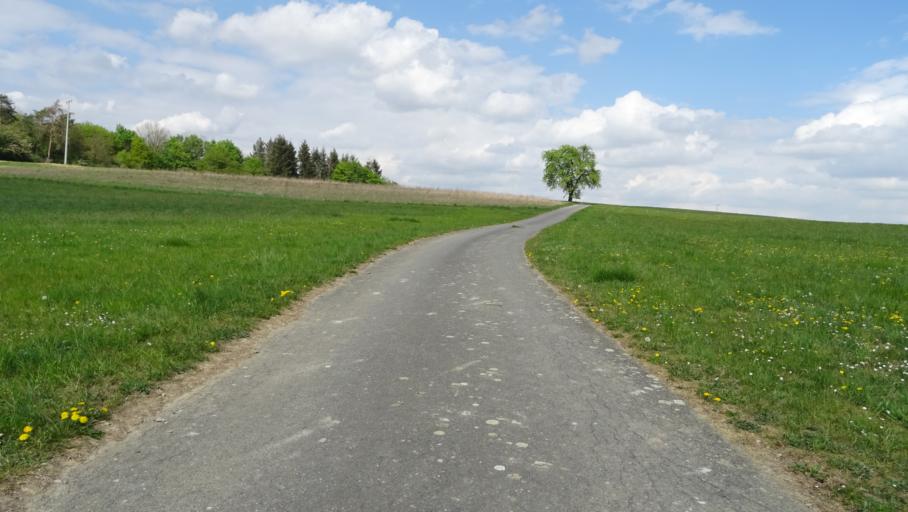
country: DE
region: Baden-Wuerttemberg
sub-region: Karlsruhe Region
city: Billigheim
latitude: 49.3996
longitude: 9.2421
